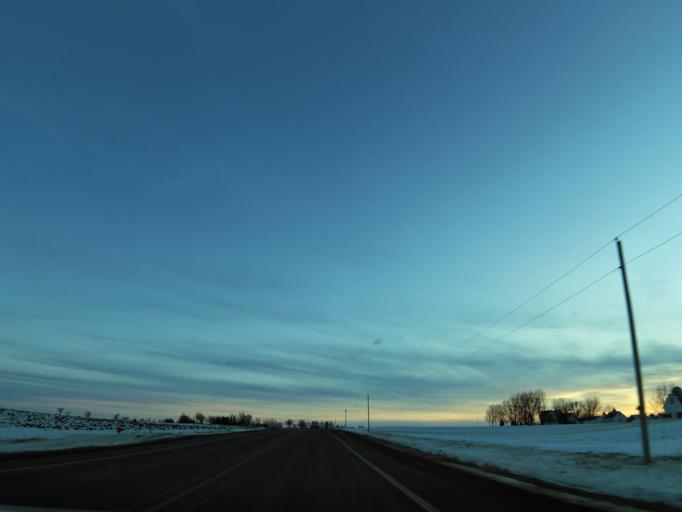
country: US
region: Minnesota
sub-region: Carver County
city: Chaska
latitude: 44.7385
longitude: -93.5622
